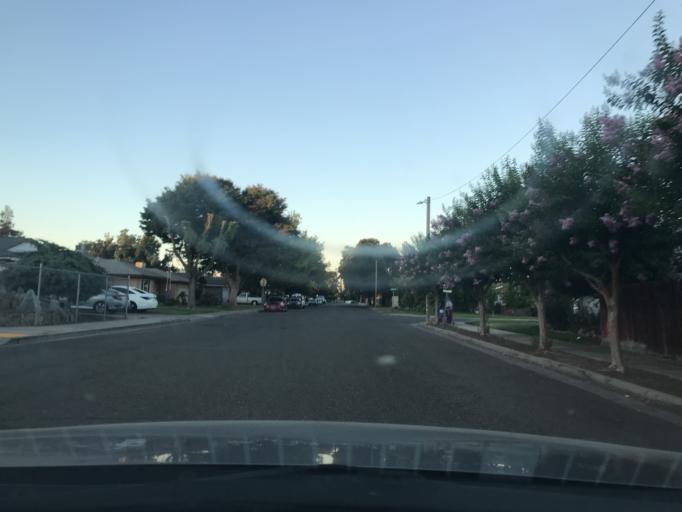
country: US
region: California
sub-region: Merced County
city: Atwater
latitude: 37.3543
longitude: -120.5981
